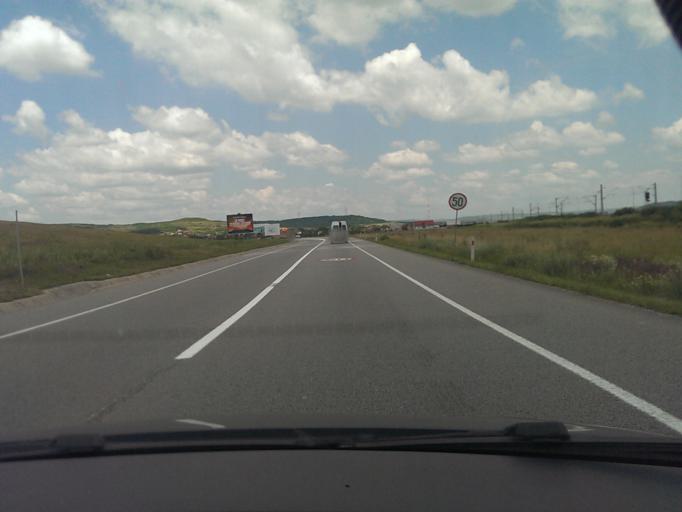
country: RO
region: Cluj
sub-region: Comuna Bontida
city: Rascruci
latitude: 46.8912
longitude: 23.7793
